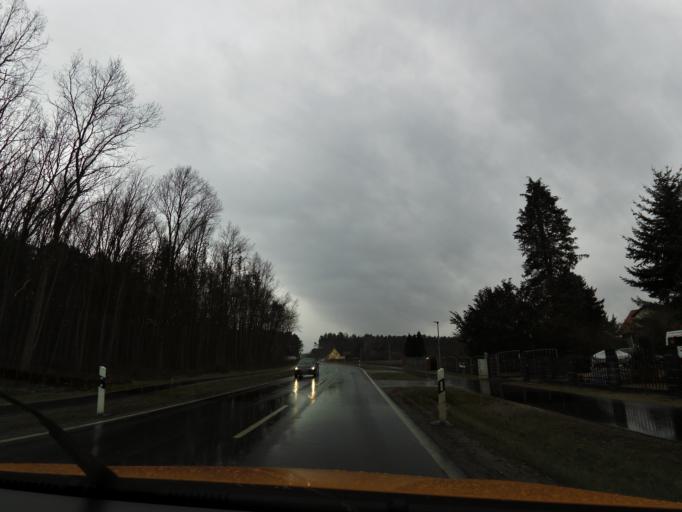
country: DE
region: Berlin
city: Lichtenrade
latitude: 52.3468
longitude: 13.4026
